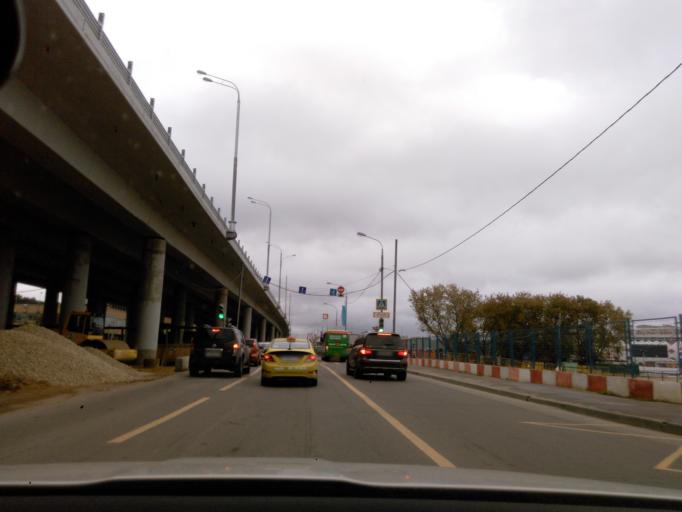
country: RU
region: Moscow
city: Strogino
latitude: 55.8244
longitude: 37.4331
